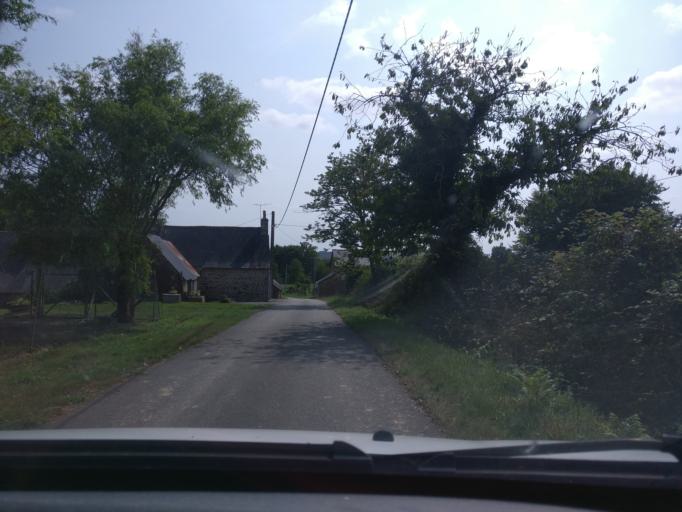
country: FR
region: Brittany
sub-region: Departement d'Ille-et-Vilaine
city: Gosne
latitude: 48.2617
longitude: -1.4798
